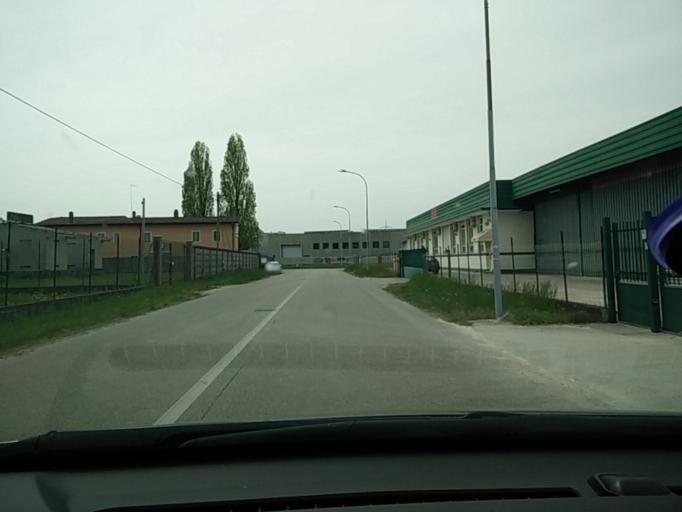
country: IT
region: Veneto
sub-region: Provincia di Venezia
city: Musile di Piave
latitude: 45.6194
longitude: 12.5363
